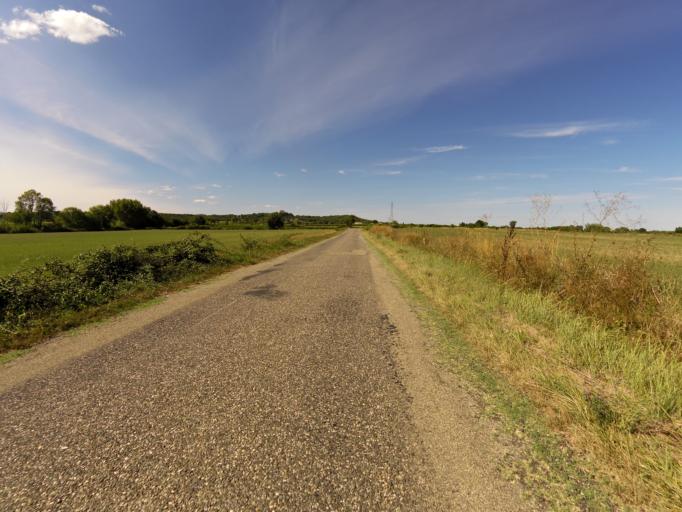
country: FR
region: Languedoc-Roussillon
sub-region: Departement du Gard
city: Lezan
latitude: 43.9649
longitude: 4.0256
